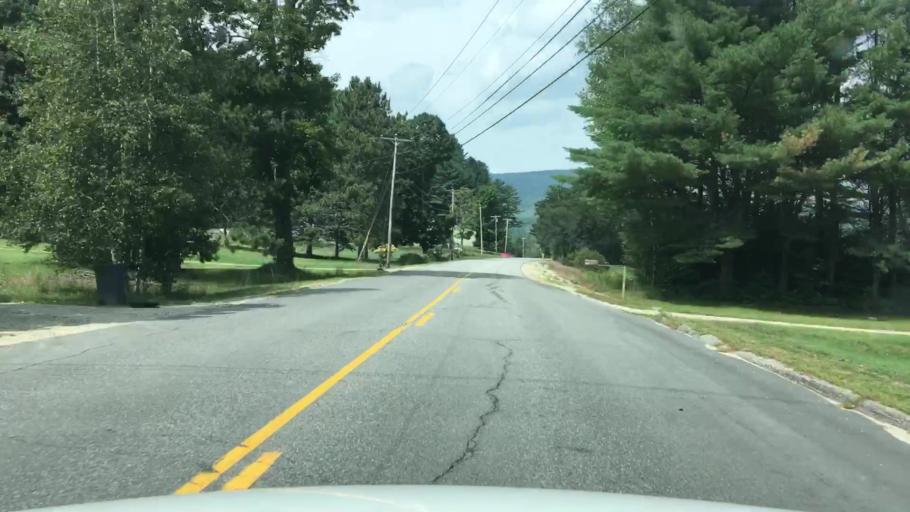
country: US
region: Maine
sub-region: Oxford County
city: Rumford
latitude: 44.5308
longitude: -70.6417
